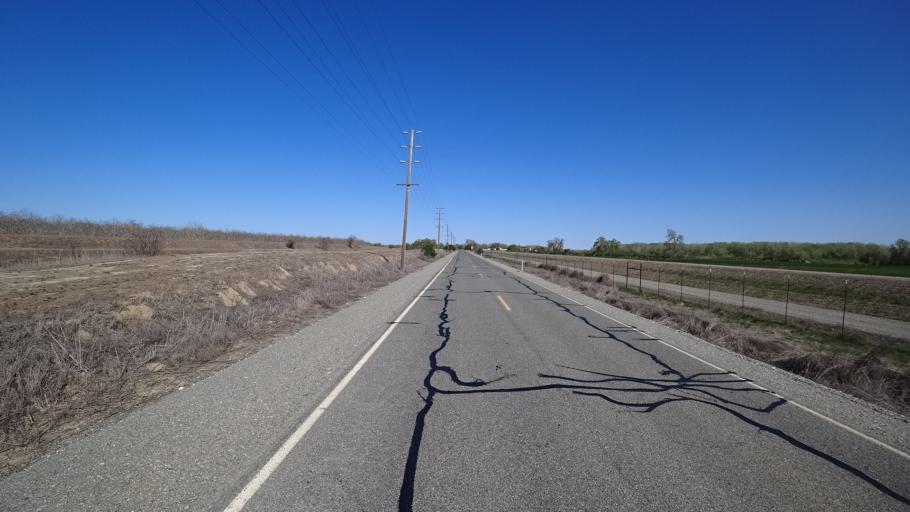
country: US
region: California
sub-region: Glenn County
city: Hamilton City
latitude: 39.7611
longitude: -122.0275
